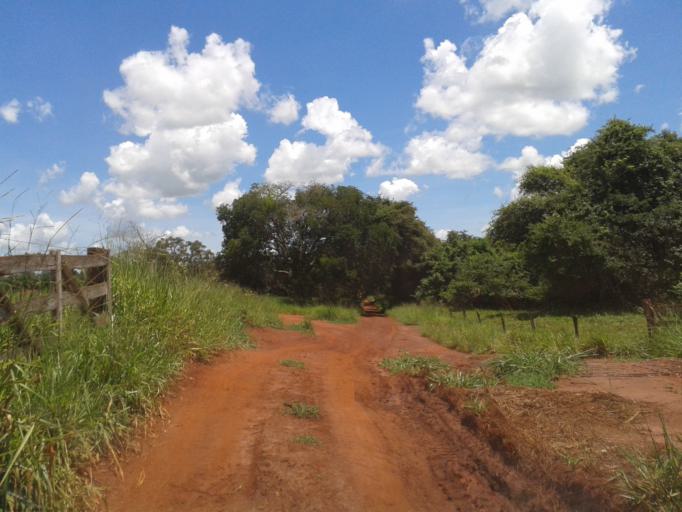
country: BR
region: Minas Gerais
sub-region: Capinopolis
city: Capinopolis
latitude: -18.7938
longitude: -49.8351
